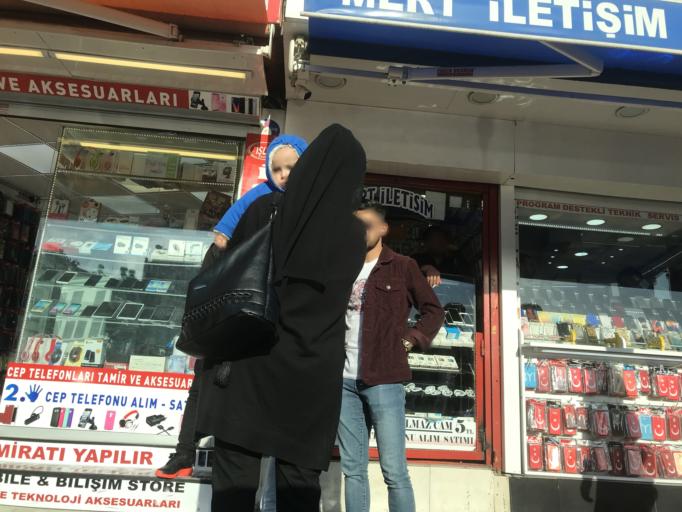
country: TR
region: Hatay
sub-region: Antakya Ilcesi
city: Antakya
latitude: 36.2035
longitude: 36.1618
